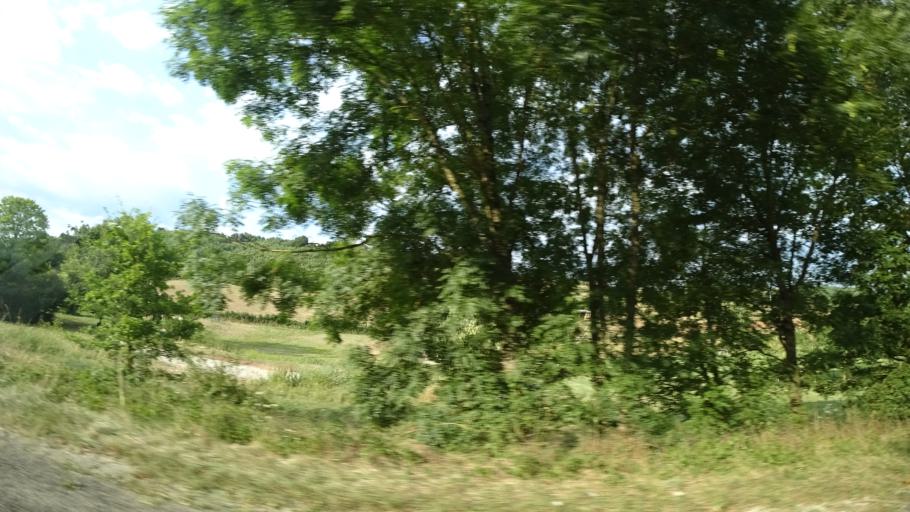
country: FR
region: Midi-Pyrenees
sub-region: Departement de l'Aveyron
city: Saint-Christophe-Vallon
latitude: 44.4843
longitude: 2.3996
